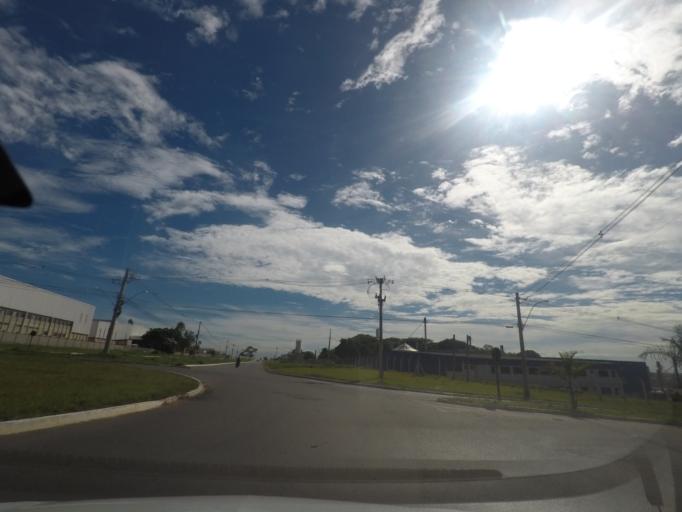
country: BR
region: Goias
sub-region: Aparecida De Goiania
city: Aparecida de Goiania
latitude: -16.8084
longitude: -49.2657
